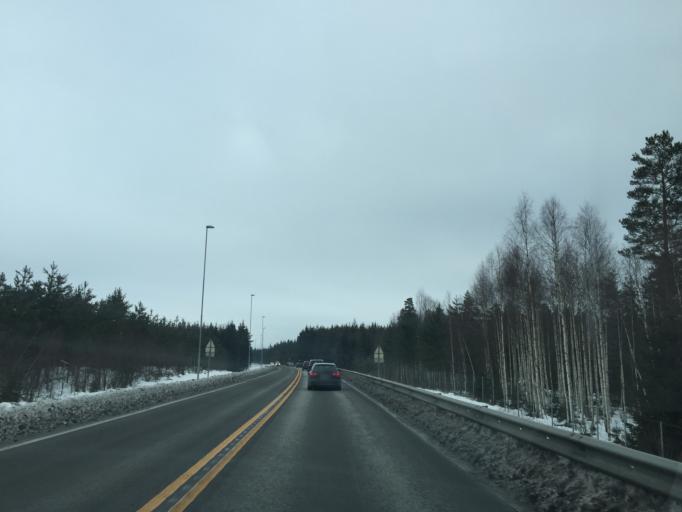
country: NO
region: Hedmark
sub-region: Loten
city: Loten
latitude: 60.7707
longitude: 11.3096
